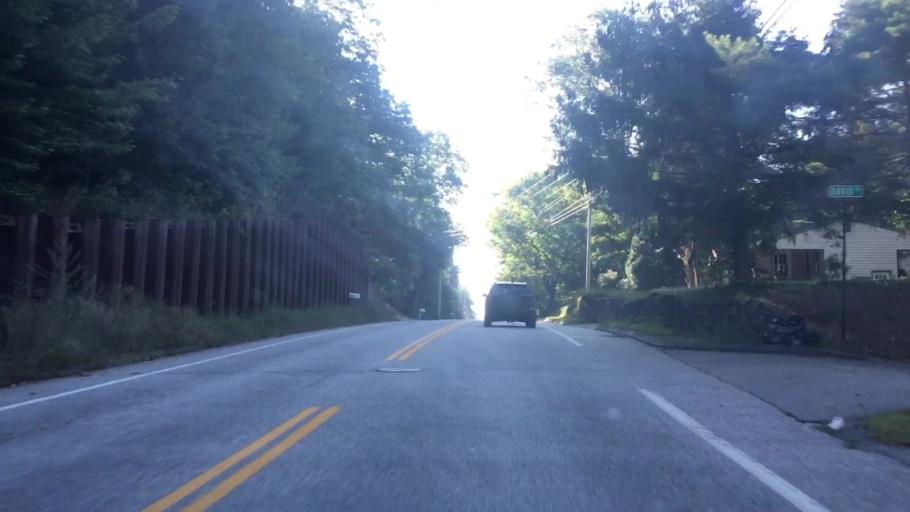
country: US
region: Maine
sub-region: Androscoggin County
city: Minot
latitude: 44.0479
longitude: -70.2736
